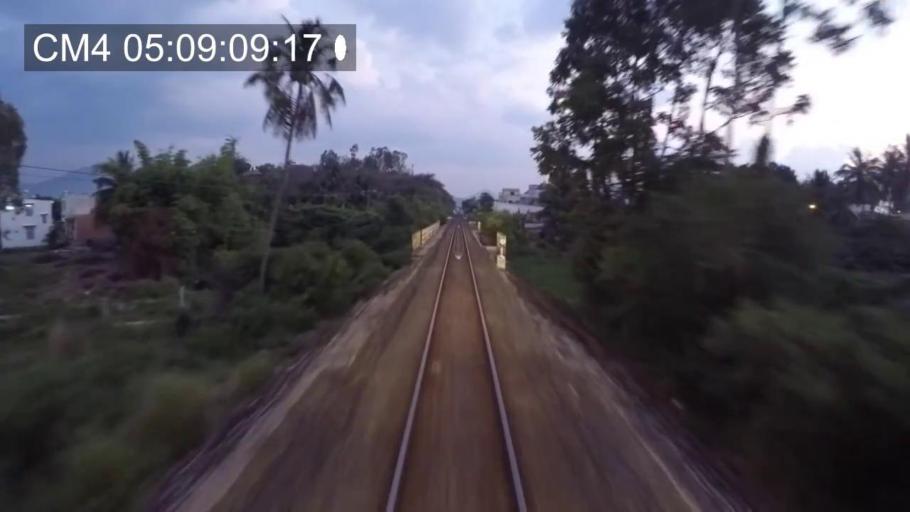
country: VN
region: Khanh Hoa
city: Nha Trang
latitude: 12.2984
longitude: 109.1860
